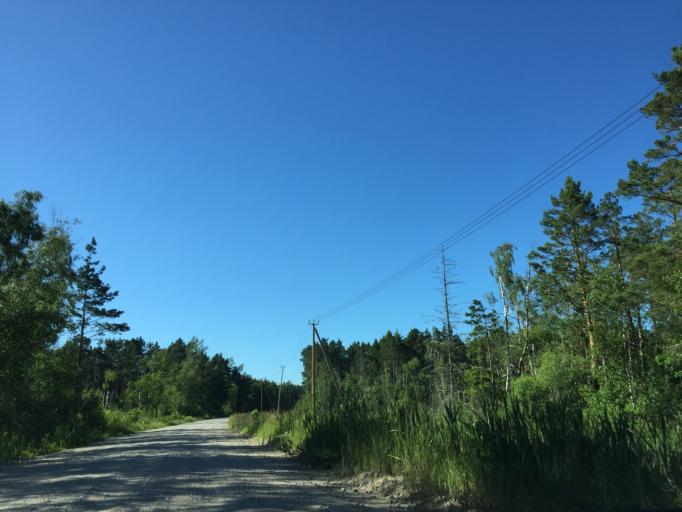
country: LV
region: Ventspils
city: Ventspils
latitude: 57.5620
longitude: 21.7272
